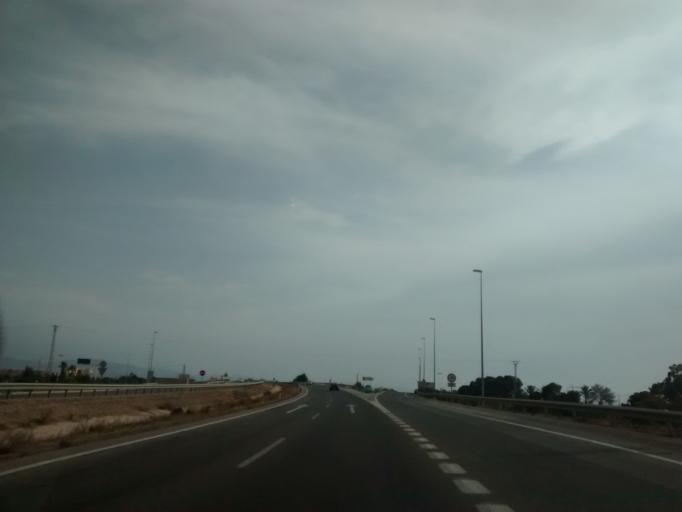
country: ES
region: Murcia
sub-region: Murcia
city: Los Alcazares
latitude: 37.7415
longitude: -0.8717
